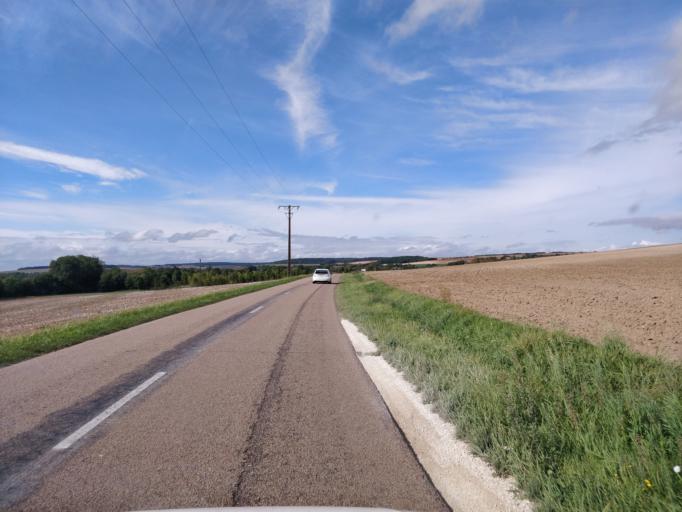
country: FR
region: Champagne-Ardenne
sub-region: Departement de l'Aube
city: Aix-en-Othe
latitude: 48.2201
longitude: 3.6196
